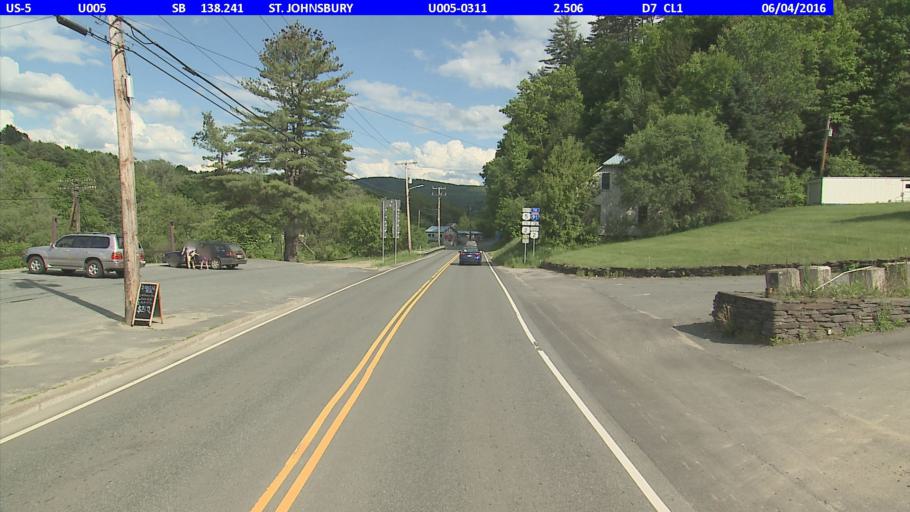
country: US
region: Vermont
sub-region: Caledonia County
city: St Johnsbury
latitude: 44.4285
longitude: -72.0174
